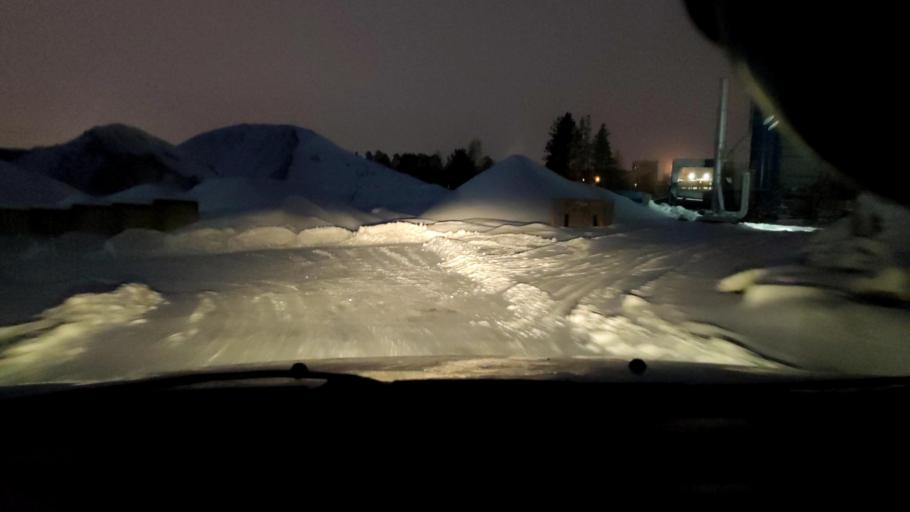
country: RU
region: Perm
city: Kondratovo
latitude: 58.0423
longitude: 56.1606
